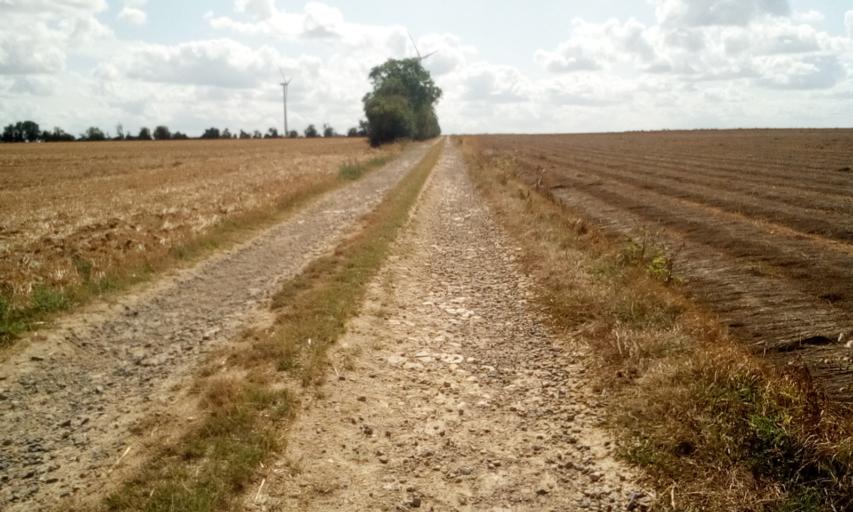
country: FR
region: Lower Normandy
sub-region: Departement du Calvados
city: Bellengreville
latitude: 49.1016
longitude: -0.2215
